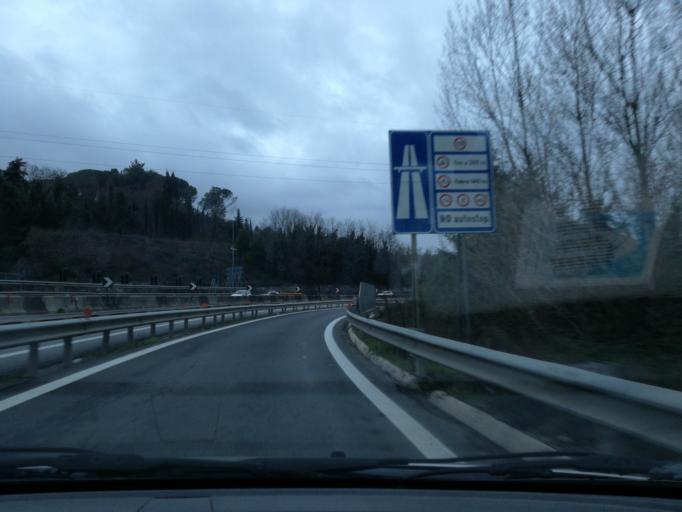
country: IT
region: Umbria
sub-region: Provincia di Perugia
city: Via Lippia
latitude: 43.0885
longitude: 12.4738
